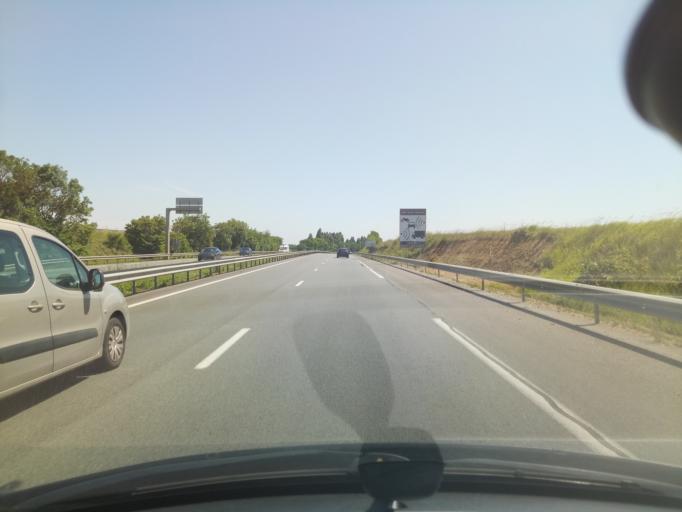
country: FR
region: Poitou-Charentes
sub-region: Departement de la Charente-Maritime
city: Dompierre-sur-Mer
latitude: 46.1981
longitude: -1.0437
